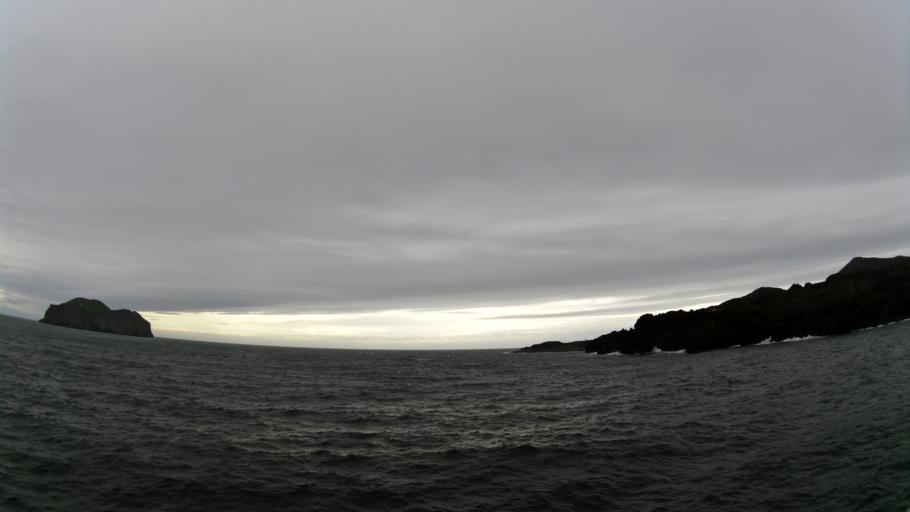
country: IS
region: South
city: Vestmannaeyjar
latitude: 63.4484
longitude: -20.2406
